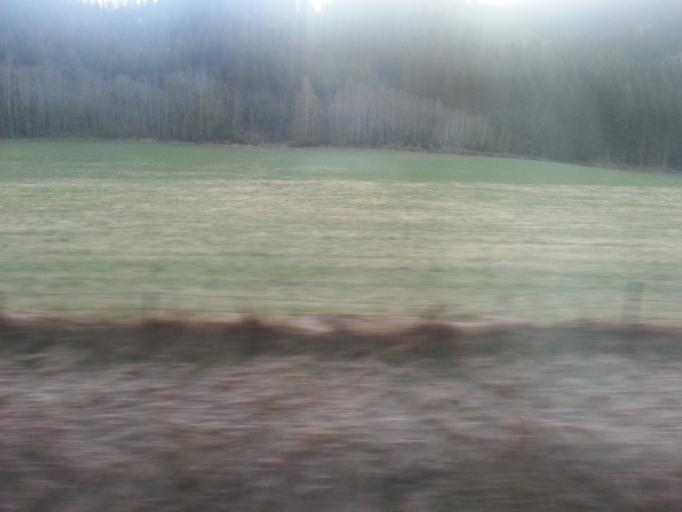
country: NO
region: Sor-Trondelag
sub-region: Melhus
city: Melhus
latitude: 63.2462
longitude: 10.2773
